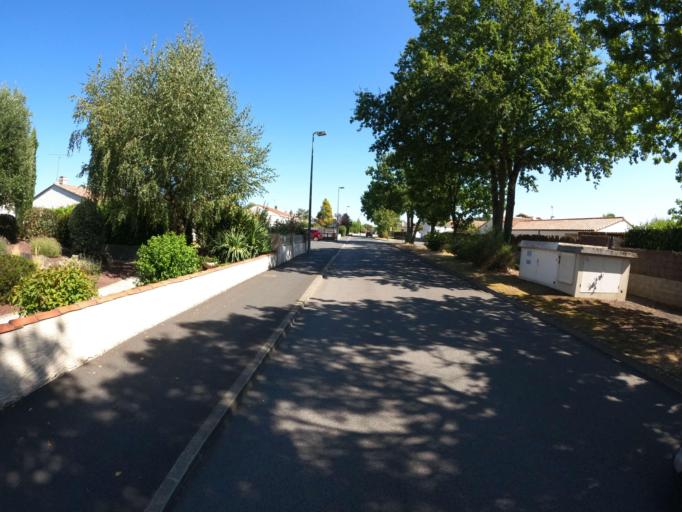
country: FR
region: Pays de la Loire
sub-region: Departement de la Vendee
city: Bouffere
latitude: 46.9619
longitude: -1.3452
